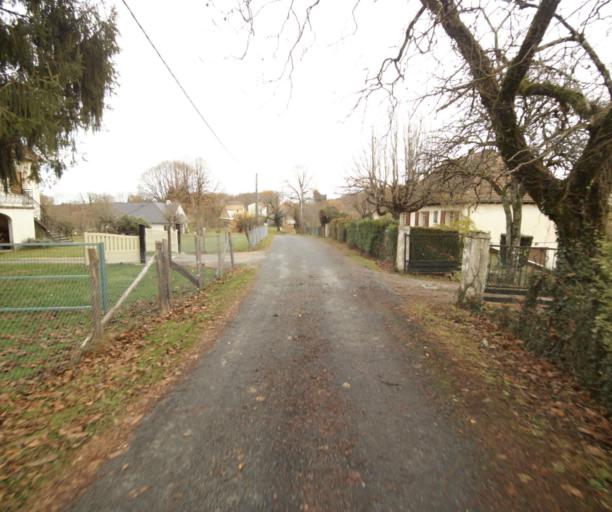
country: FR
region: Limousin
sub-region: Departement de la Correze
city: Sainte-Fortunade
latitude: 45.1745
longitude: 1.7517
